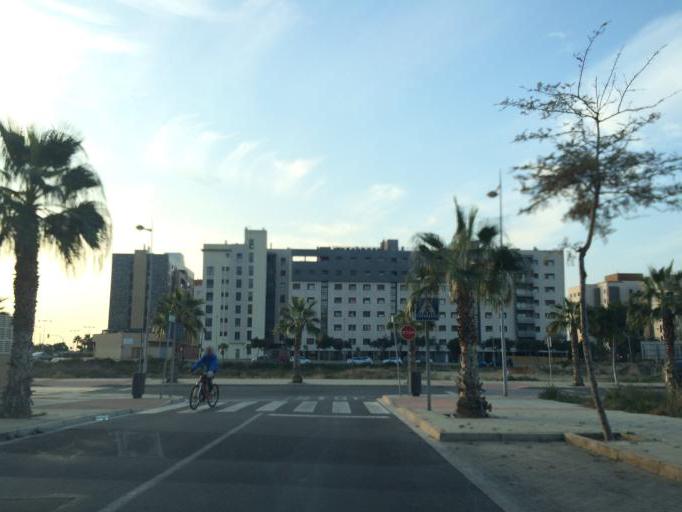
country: ES
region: Andalusia
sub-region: Provincia de Almeria
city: Almeria
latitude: 36.8336
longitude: -2.4392
